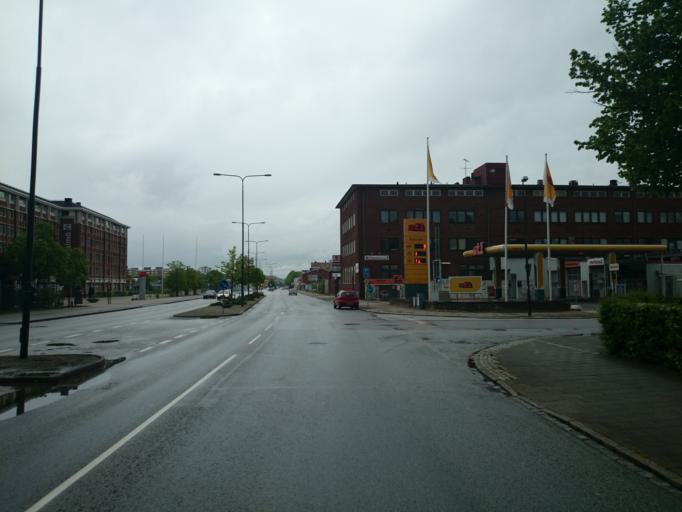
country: SE
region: Skane
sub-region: Malmo
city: Malmoe
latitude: 55.5976
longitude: 13.0241
